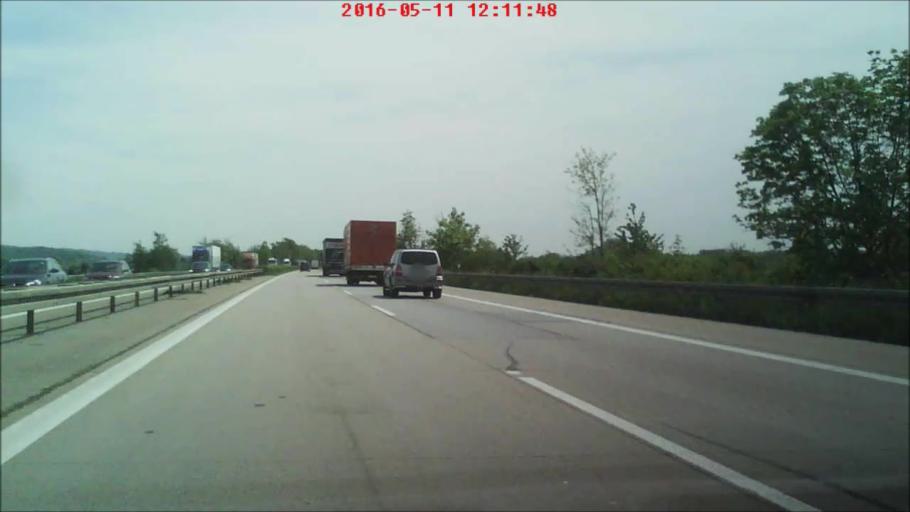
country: DE
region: Bavaria
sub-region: Lower Bavaria
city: Offenberg
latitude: 48.8539
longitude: 12.8740
